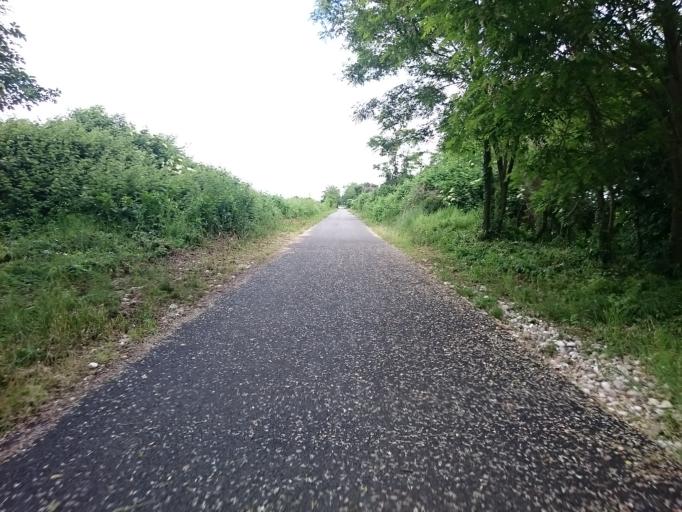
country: IT
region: Veneto
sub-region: Provincia di Padova
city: Campodoro
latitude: 45.5064
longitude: 11.7475
